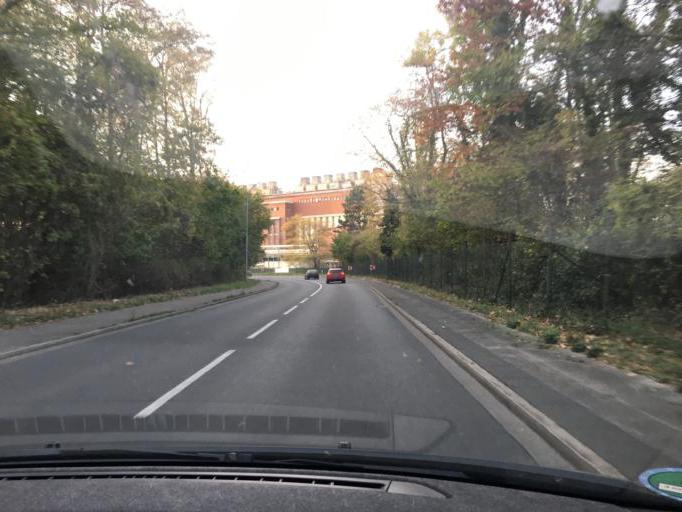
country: DE
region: North Rhine-Westphalia
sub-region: Regierungsbezirk Koln
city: Hurth
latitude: 50.8630
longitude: 6.8289
